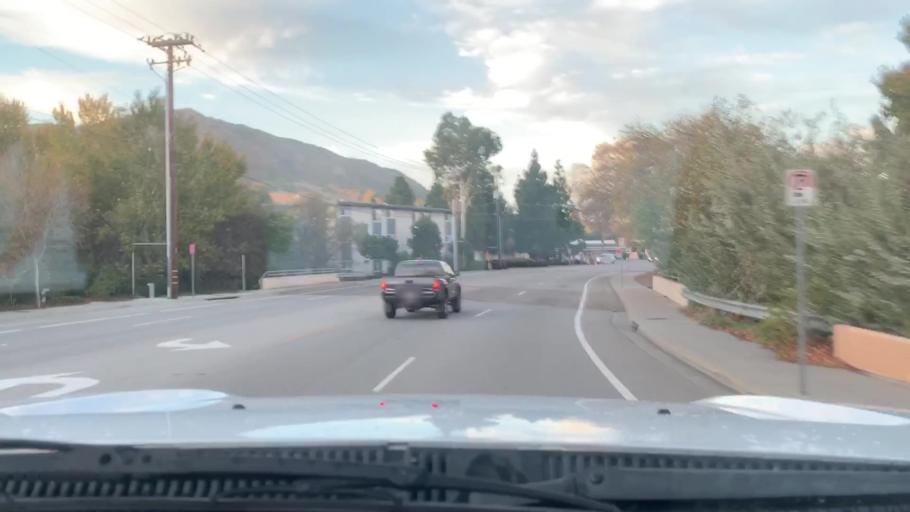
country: US
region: California
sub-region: San Luis Obispo County
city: San Luis Obispo
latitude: 35.2943
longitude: -120.6660
